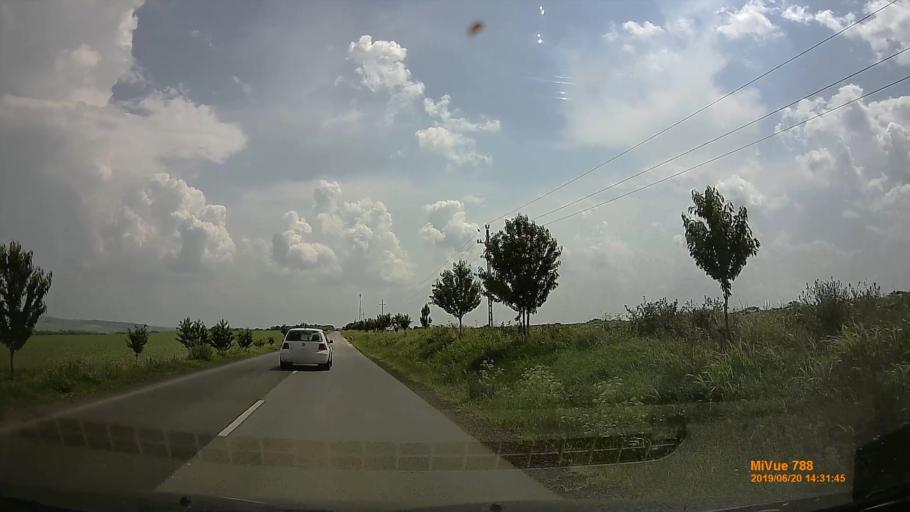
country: HU
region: Baranya
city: Hosszuheteny
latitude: 46.1347
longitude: 18.3480
